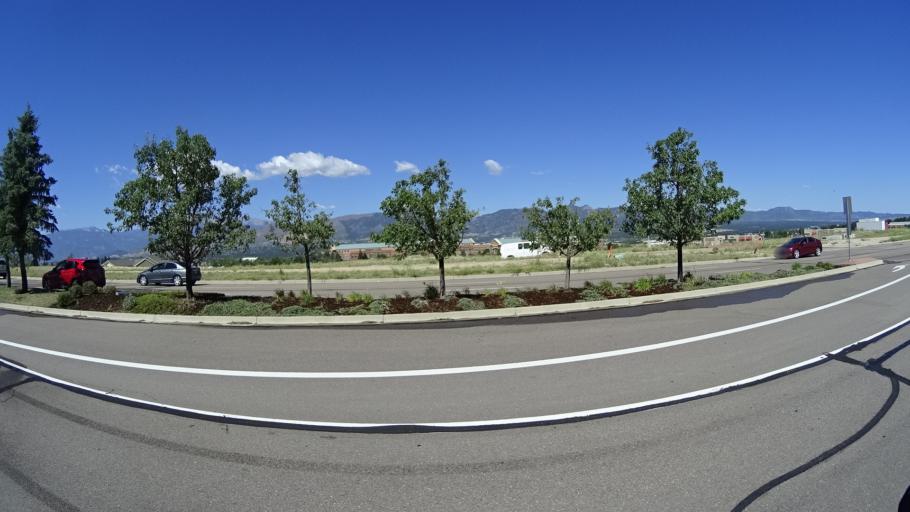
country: US
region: Colorado
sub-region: El Paso County
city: Air Force Academy
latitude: 38.9632
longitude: -104.7845
